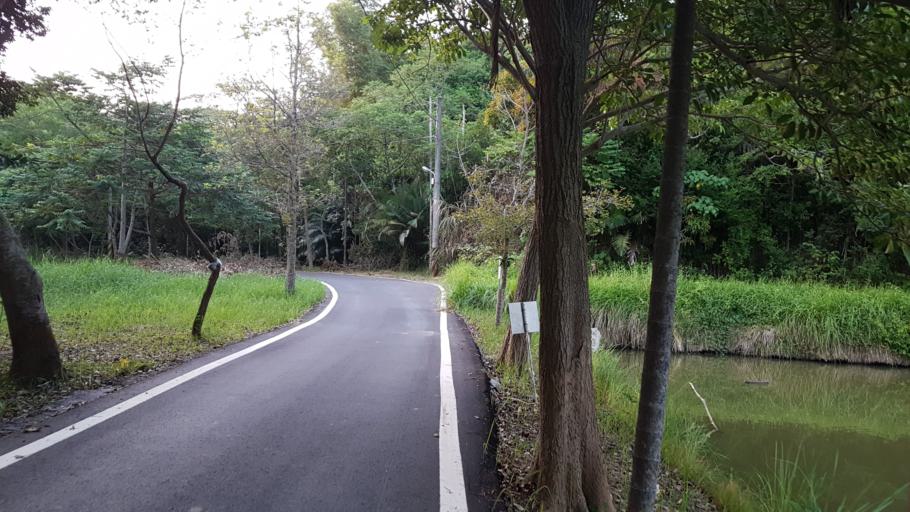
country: TW
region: Taiwan
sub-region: Chiayi
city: Jiayi Shi
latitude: 23.3620
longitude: 120.4679
